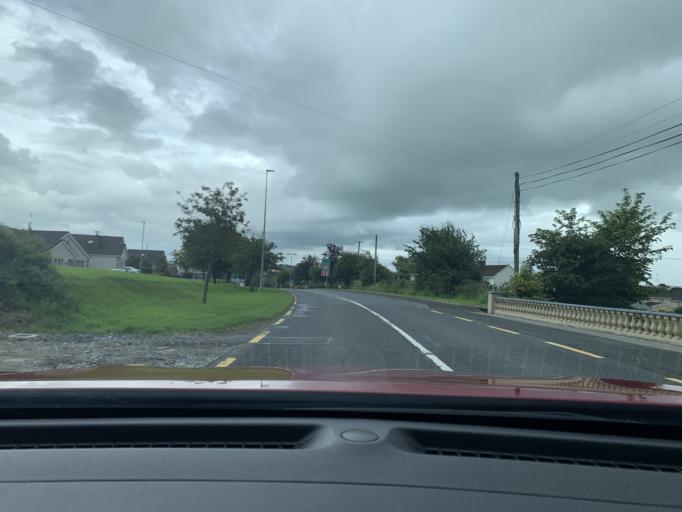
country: IE
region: Ulster
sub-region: County Donegal
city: Raphoe
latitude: 54.8027
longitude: -7.5999
